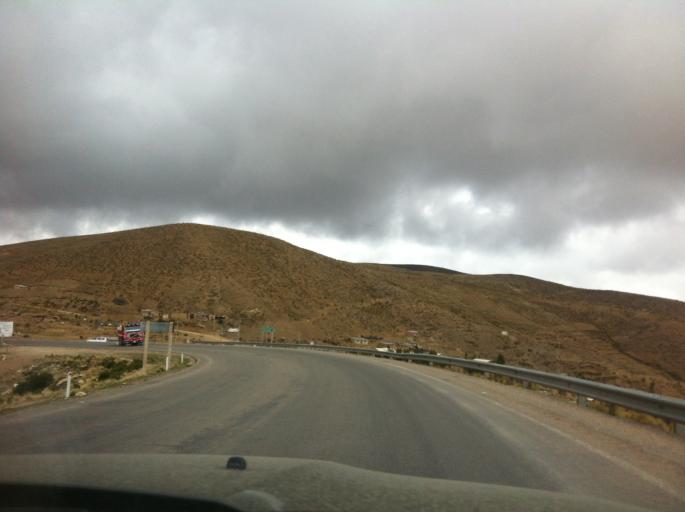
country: BO
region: Cochabamba
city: Irpa Irpa
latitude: -17.6866
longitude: -66.5082
